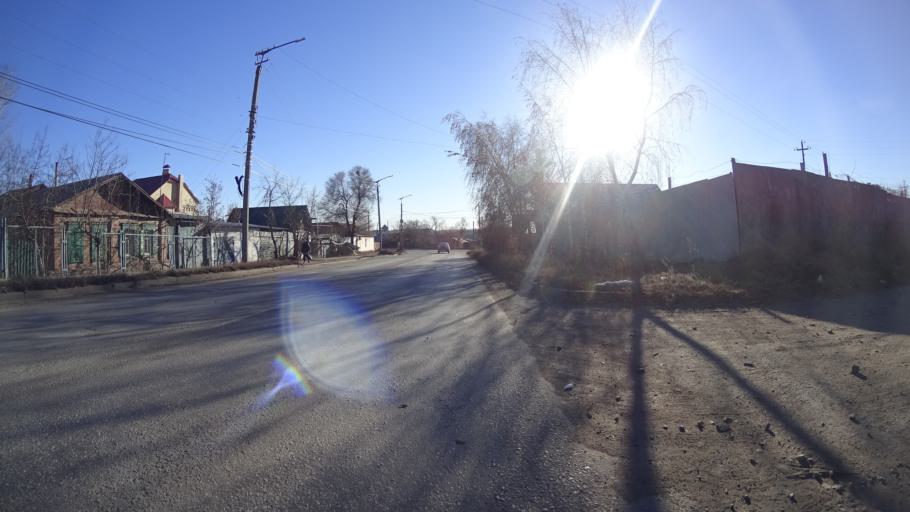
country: RU
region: Chelyabinsk
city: Troitsk
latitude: 54.0974
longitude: 61.5628
